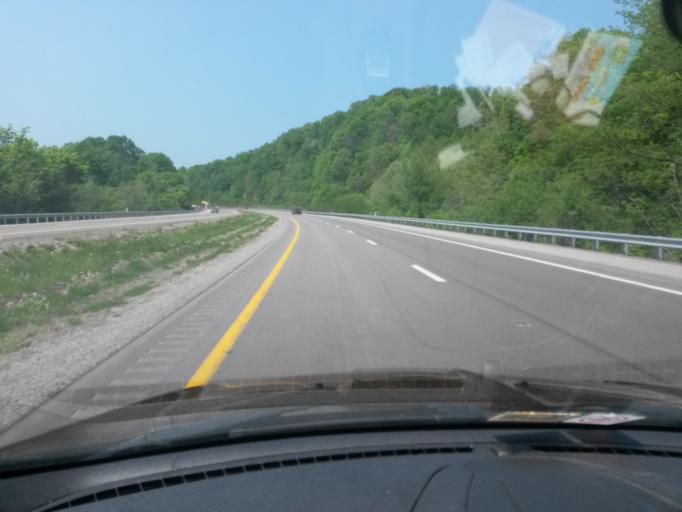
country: US
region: West Virginia
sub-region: Lewis County
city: Weston
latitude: 38.9022
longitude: -80.6166
